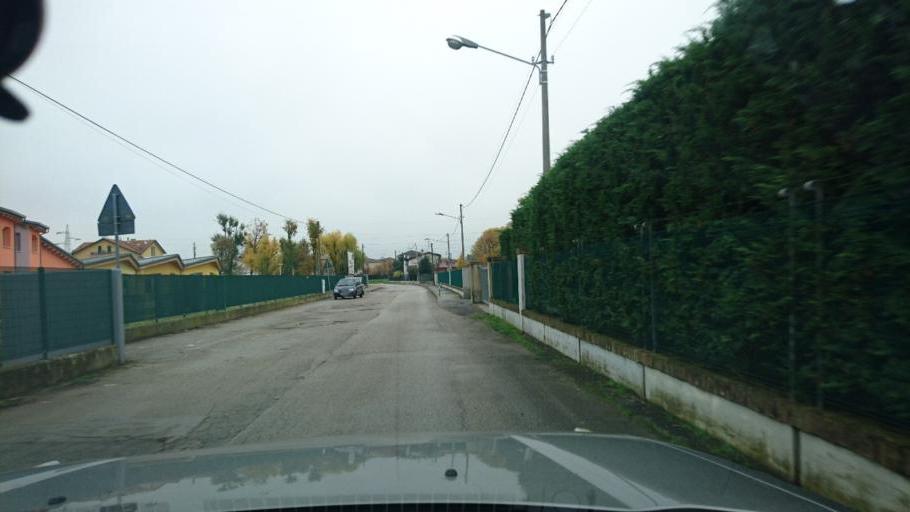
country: IT
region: Veneto
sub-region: Provincia di Padova
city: Padova
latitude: 45.4310
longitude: 11.8672
